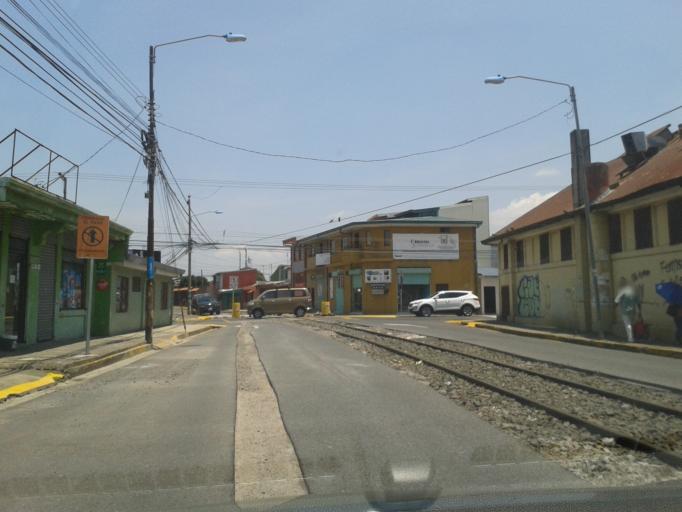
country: CR
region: Heredia
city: San Francisco
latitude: 9.9952
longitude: -84.1231
